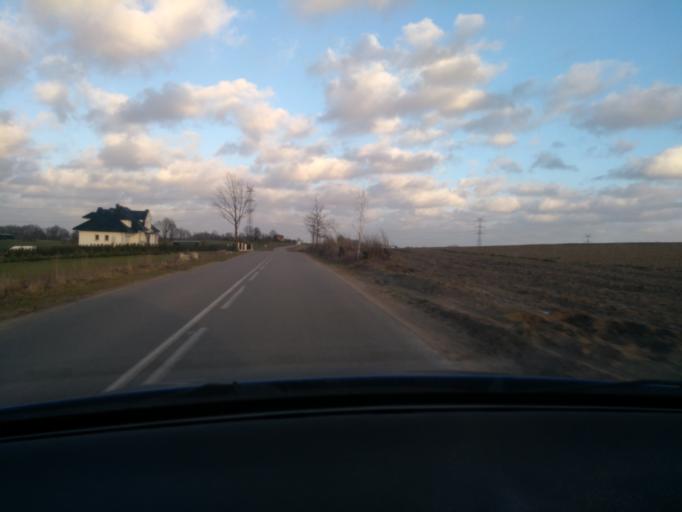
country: PL
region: Pomeranian Voivodeship
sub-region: Powiat kartuski
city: Przodkowo
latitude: 54.4171
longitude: 18.2885
